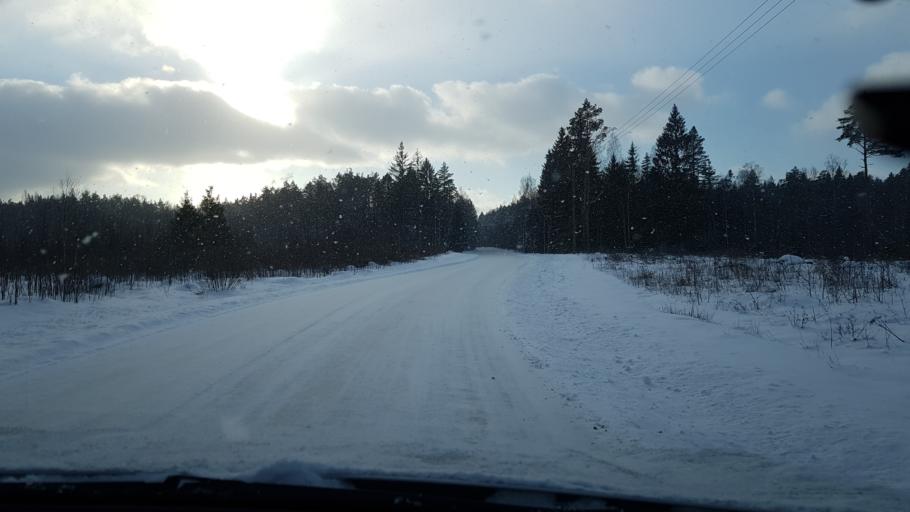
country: EE
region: Harju
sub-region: Nissi vald
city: Turba
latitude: 59.1805
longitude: 24.1349
